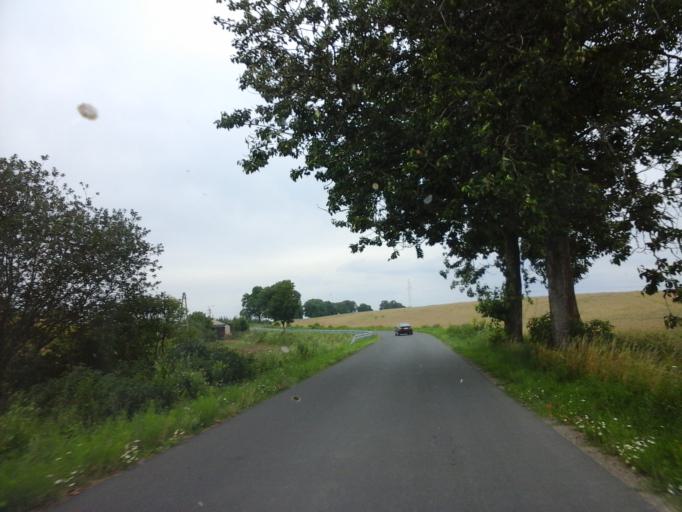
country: PL
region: West Pomeranian Voivodeship
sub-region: Powiat choszczenski
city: Krzecin
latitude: 53.0864
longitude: 15.5392
